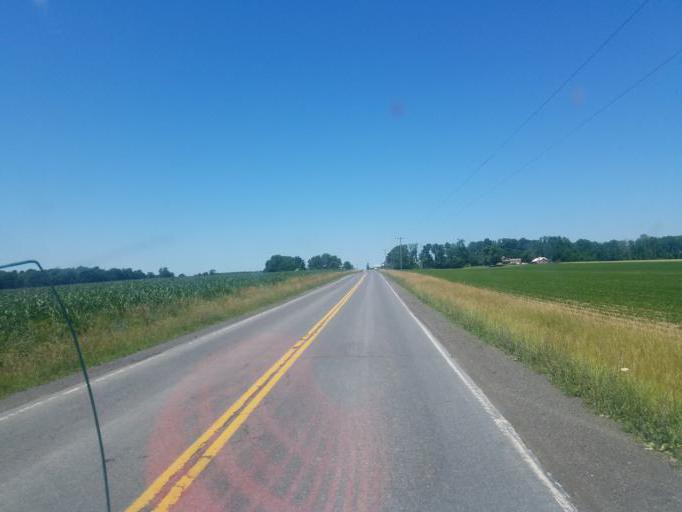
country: US
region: New York
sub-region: Yates County
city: Penn Yan
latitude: 42.7183
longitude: -76.9975
